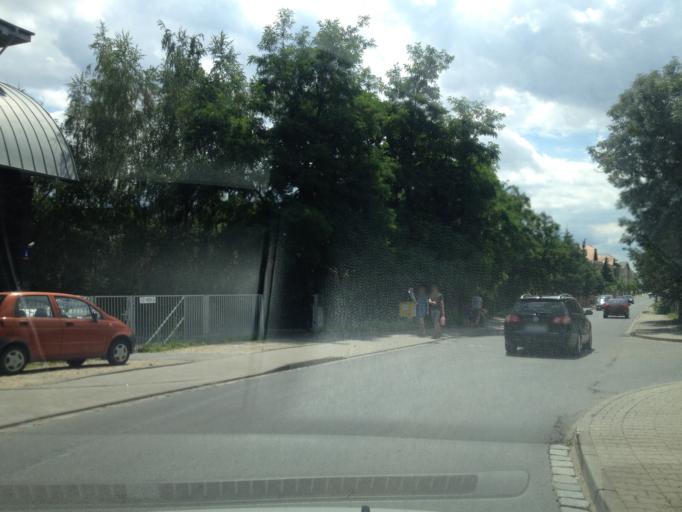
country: PL
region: Lower Silesian Voivodeship
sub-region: Powiat wroclawski
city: Smolec
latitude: 51.0984
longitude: 16.9370
